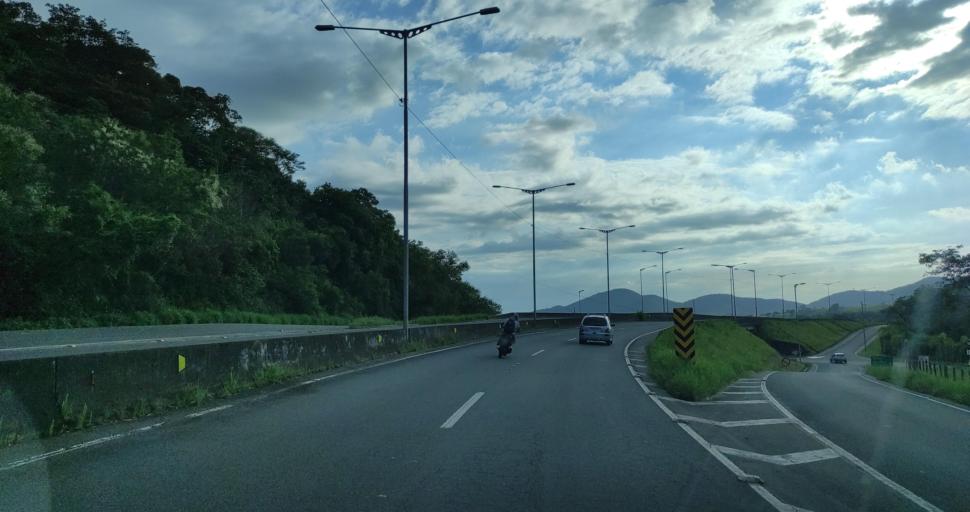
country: BR
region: Santa Catarina
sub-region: Penha
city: Penha
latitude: -26.8051
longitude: -48.6462
